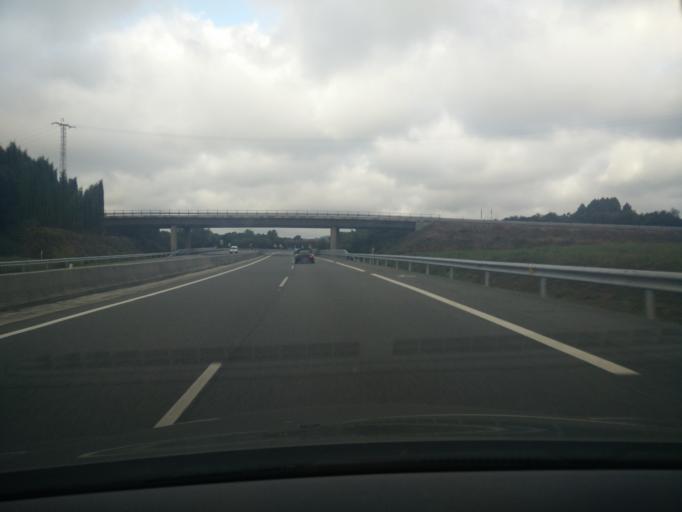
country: ES
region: Galicia
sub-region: Provincia da Coruna
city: Laracha
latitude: 43.2554
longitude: -8.6107
